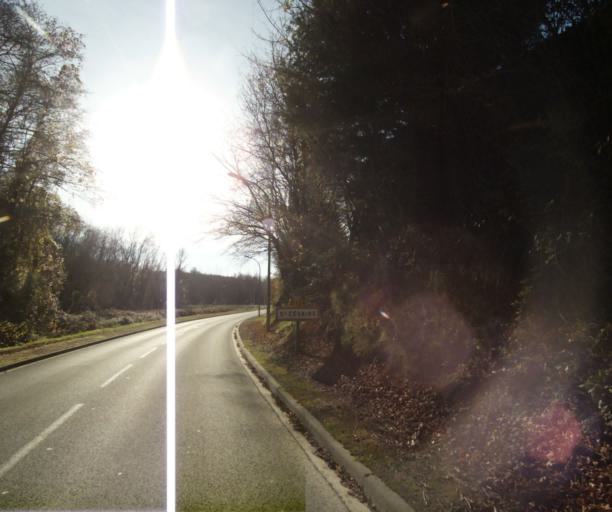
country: FR
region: Poitou-Charentes
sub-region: Departement de la Charente-Maritime
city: Chaniers
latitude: 45.7562
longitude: -0.5037
